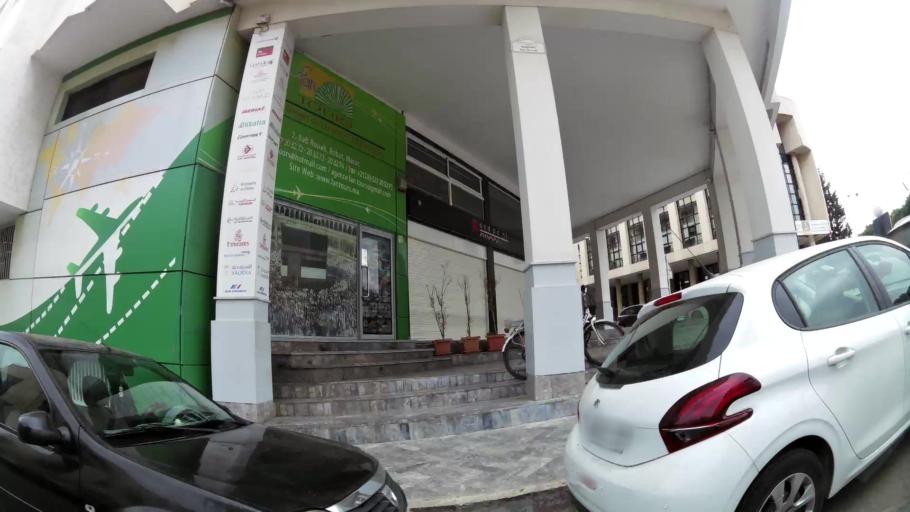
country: MA
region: Rabat-Sale-Zemmour-Zaer
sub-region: Rabat
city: Rabat
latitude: 34.0135
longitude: -6.8373
